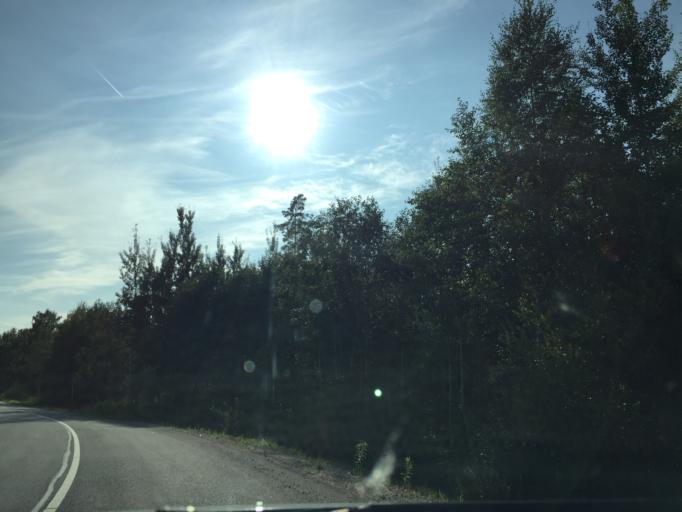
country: LV
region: Kegums
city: Kegums
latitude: 56.8231
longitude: 24.7552
